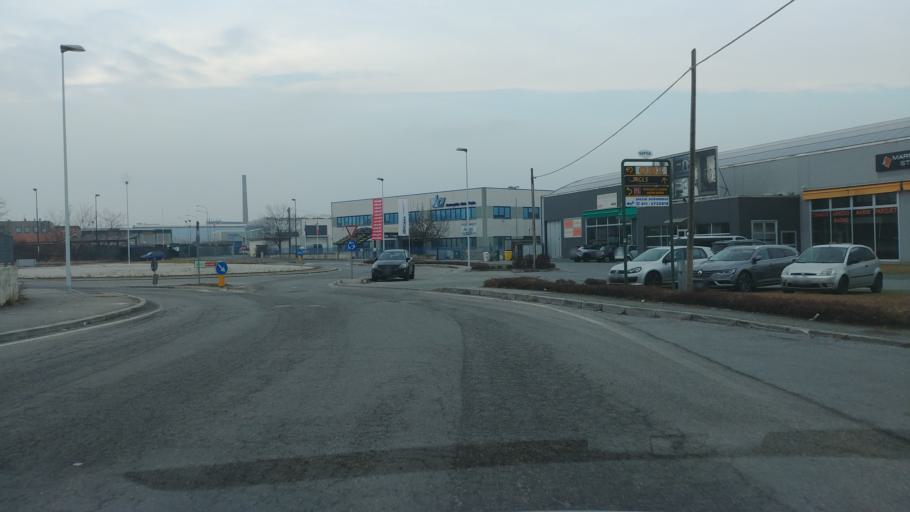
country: IT
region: Piedmont
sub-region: Provincia di Cuneo
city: Roata Rossi
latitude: 44.4248
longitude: 7.5543
